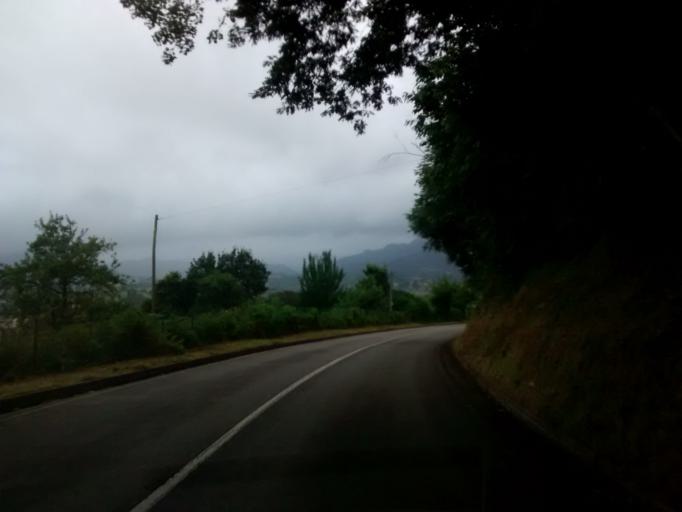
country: ES
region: Asturias
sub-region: Province of Asturias
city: Villaviciosa
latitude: 43.5301
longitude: -5.3899
